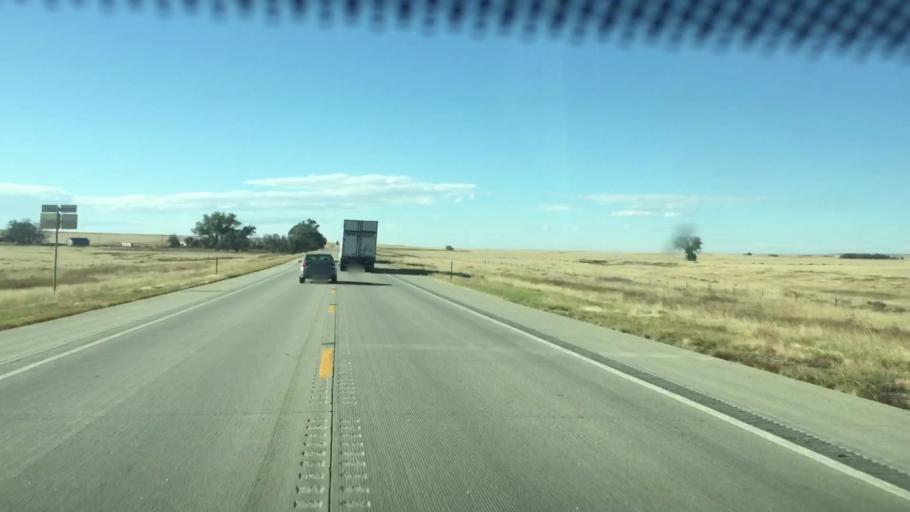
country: US
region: Colorado
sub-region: Lincoln County
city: Hugo
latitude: 38.9337
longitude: -103.2017
